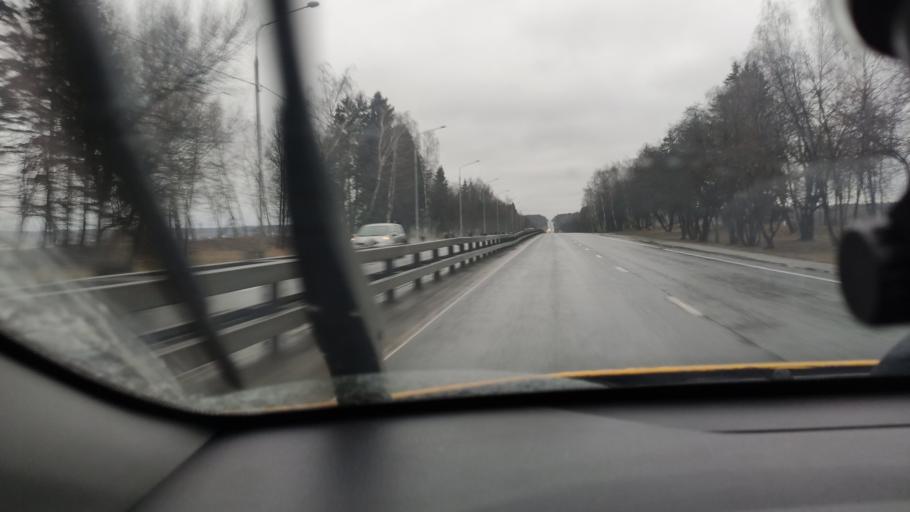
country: RU
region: Moskovskaya
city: Troitsk
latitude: 55.3316
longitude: 37.2854
